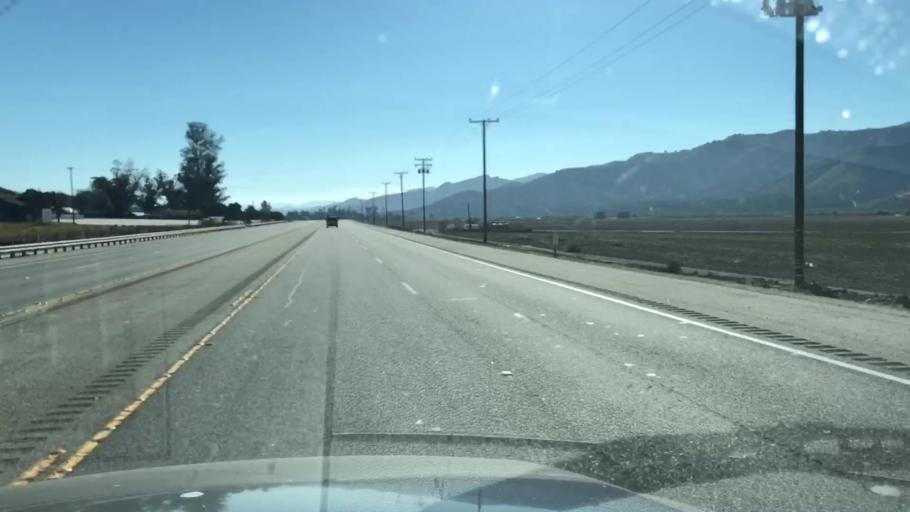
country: US
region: California
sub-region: Ventura County
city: Piru
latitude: 34.4083
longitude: -118.7751
